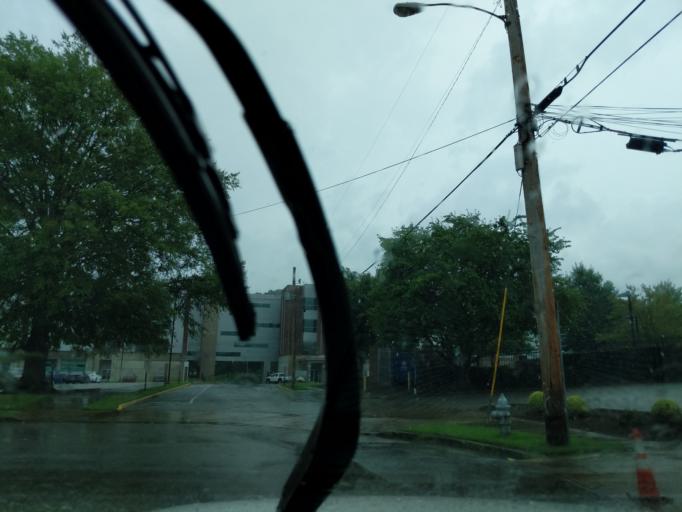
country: US
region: Tennessee
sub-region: Shelby County
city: Memphis
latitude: 35.1400
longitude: -90.0375
